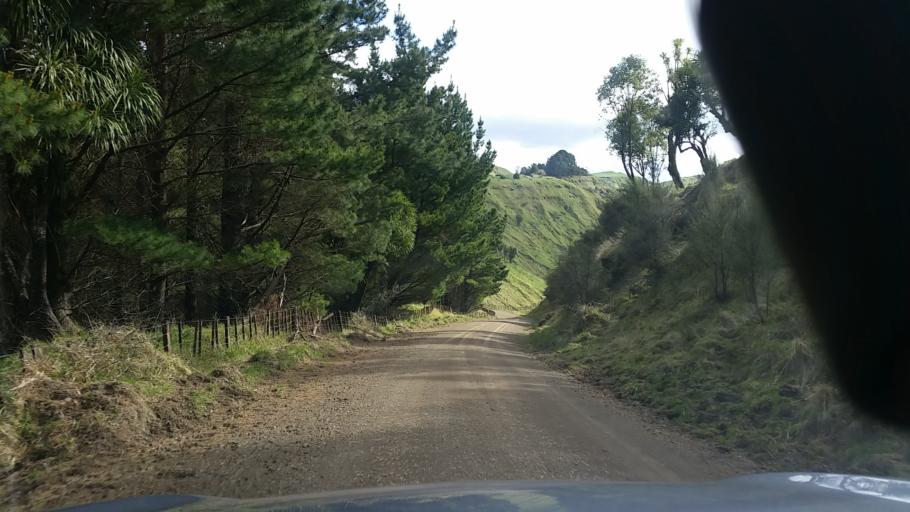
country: NZ
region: Hawke's Bay
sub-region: Napier City
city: Napier
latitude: -39.2172
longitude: 176.9774
